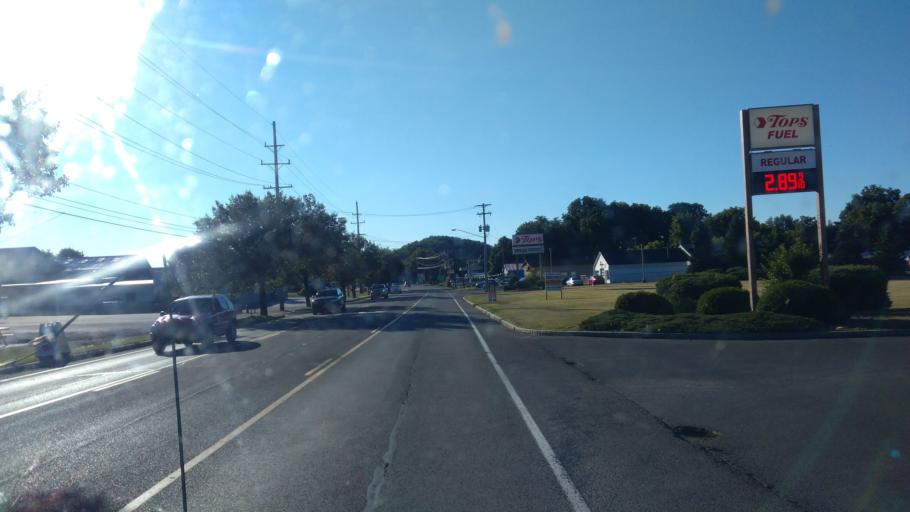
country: US
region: New York
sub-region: Wayne County
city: Lyons
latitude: 43.0602
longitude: -76.9960
